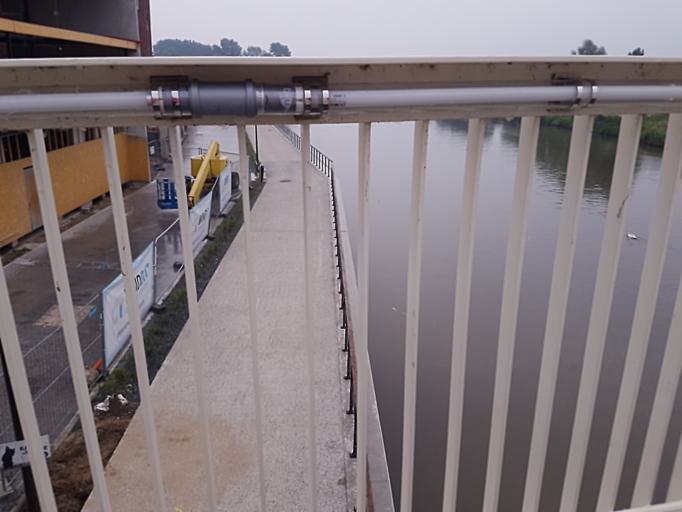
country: FR
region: Nord-Pas-de-Calais
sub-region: Departement du Nord
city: Wervicq-Sud
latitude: 50.7764
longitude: 3.0429
